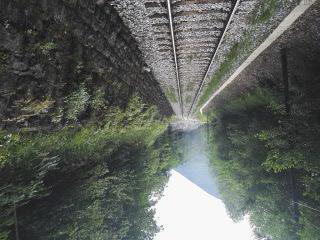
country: SI
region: Cerkno
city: Cerkno
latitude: 46.1617
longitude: 13.8748
